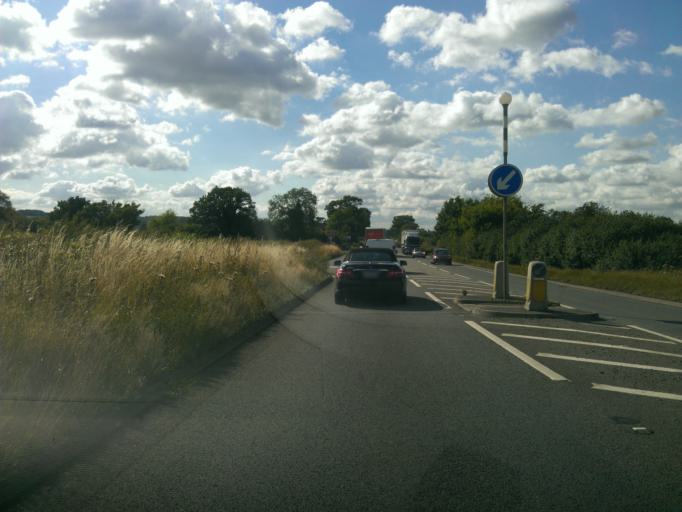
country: GB
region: England
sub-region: Warwickshire
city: Hartshill
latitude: 52.5638
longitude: -1.5009
